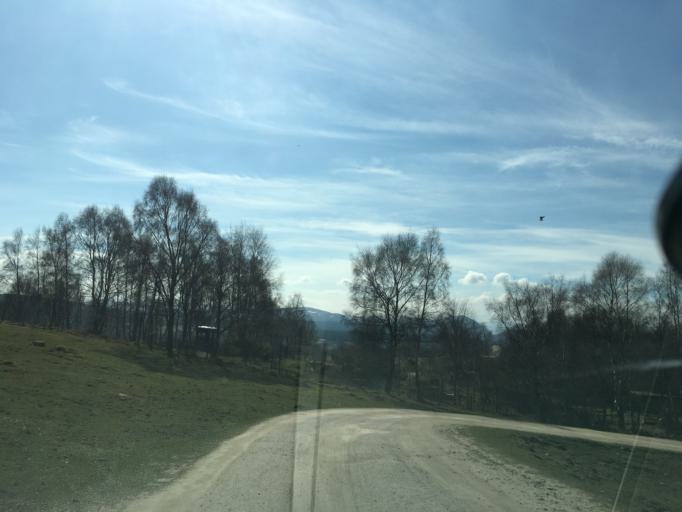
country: GB
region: Scotland
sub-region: Highland
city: Kingussie
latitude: 57.1085
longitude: -3.9791
